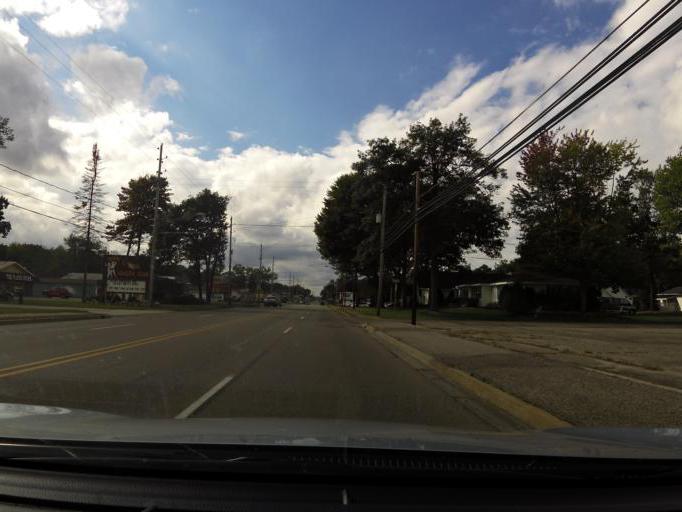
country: US
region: Michigan
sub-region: Roscommon County
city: Prudenville
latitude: 44.2987
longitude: -84.6946
